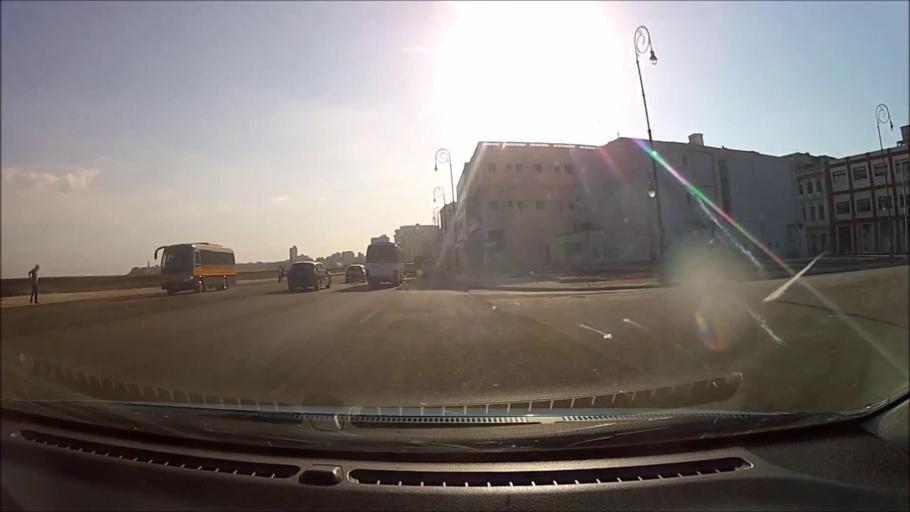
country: CU
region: La Habana
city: Centro Habana
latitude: 23.1417
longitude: -82.3711
